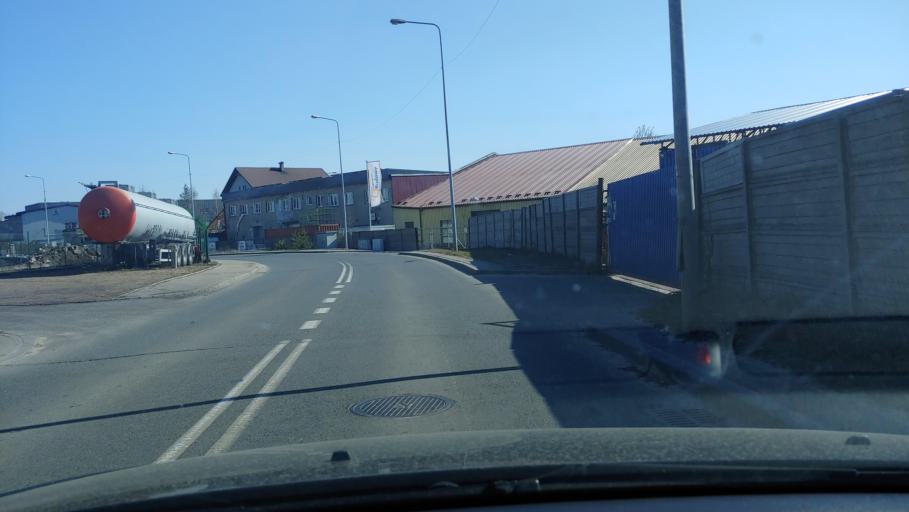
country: PL
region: Lesser Poland Voivodeship
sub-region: Powiat chrzanowski
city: Trzebinia
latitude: 50.1545
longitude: 19.4578
